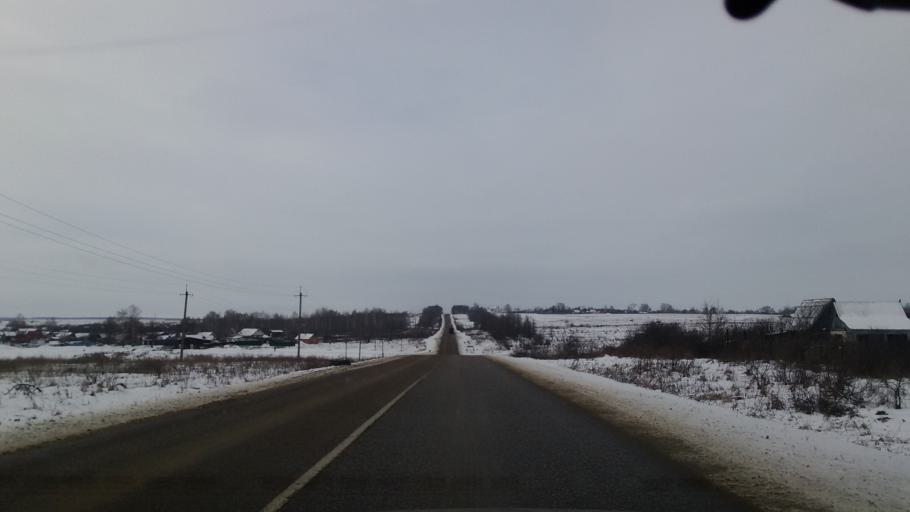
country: RU
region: Tula
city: Bogoroditsk
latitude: 53.7637
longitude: 38.0919
